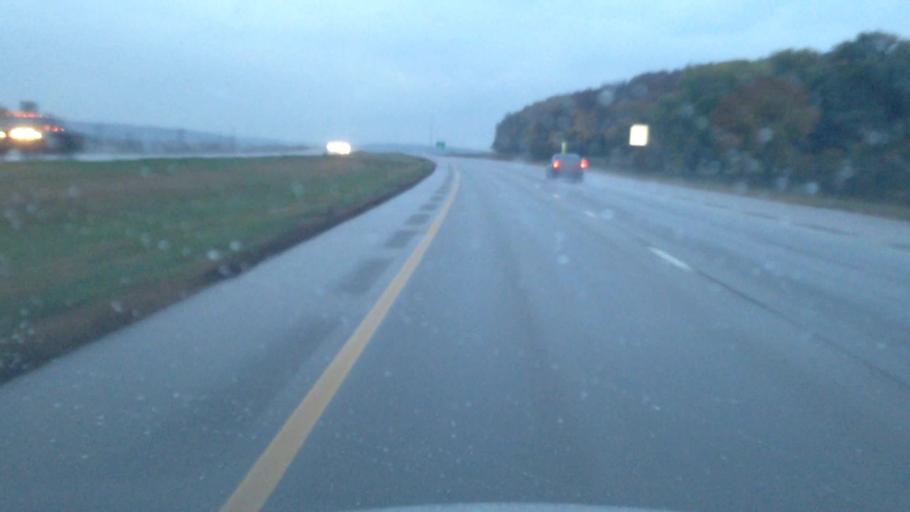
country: US
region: Kansas
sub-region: Douglas County
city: Lawrence
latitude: 38.8927
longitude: -95.2606
